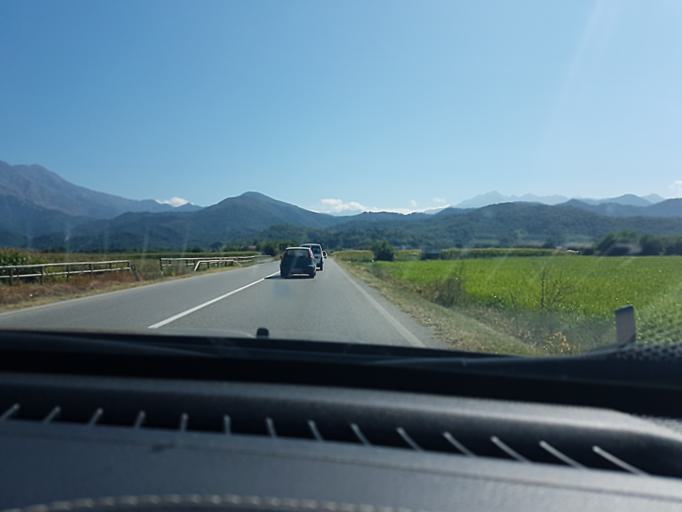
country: IT
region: Piedmont
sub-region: Provincia di Cuneo
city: Boves
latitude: 44.3460
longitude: 7.5458
